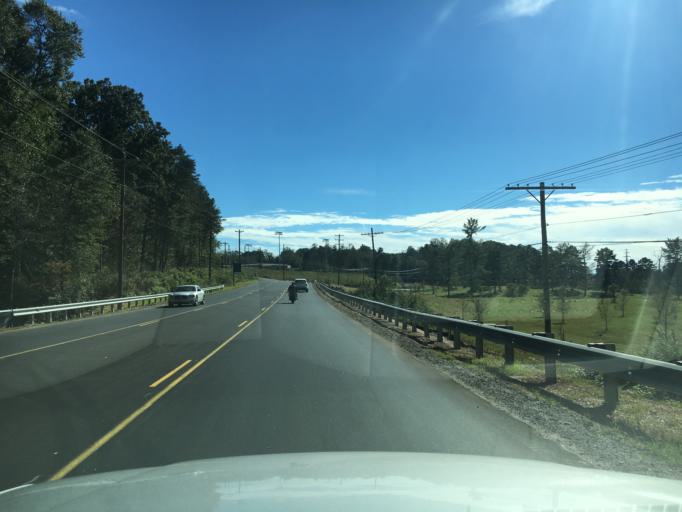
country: US
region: North Carolina
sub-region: Burke County
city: Morganton
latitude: 35.7579
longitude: -81.7030
